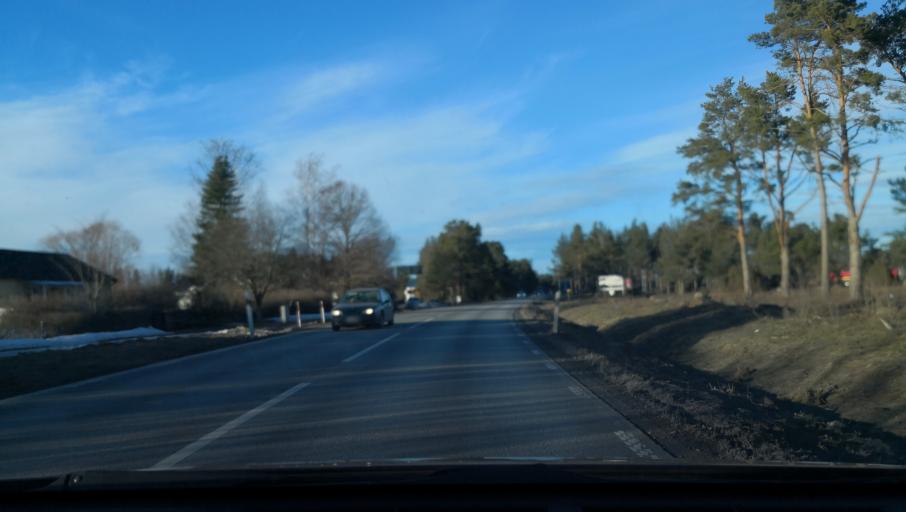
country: SE
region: Uppsala
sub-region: Osthammars Kommun
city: OEsthammar
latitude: 60.2454
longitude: 18.3478
